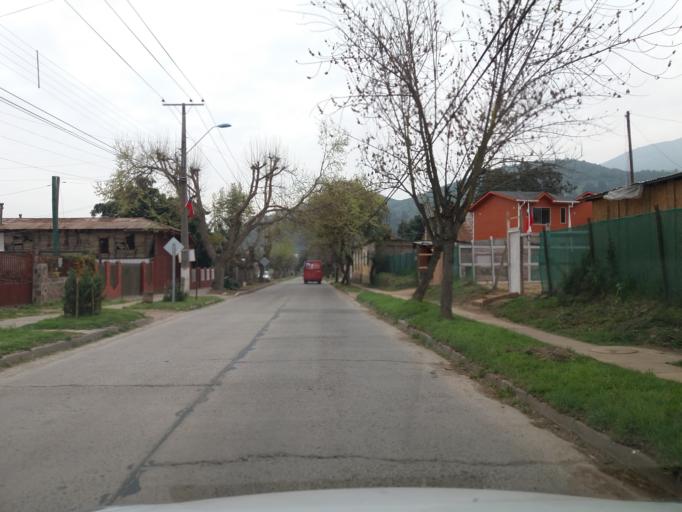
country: CL
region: Valparaiso
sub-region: Provincia de Quillota
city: Hacienda La Calera
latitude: -32.7949
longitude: -71.1479
